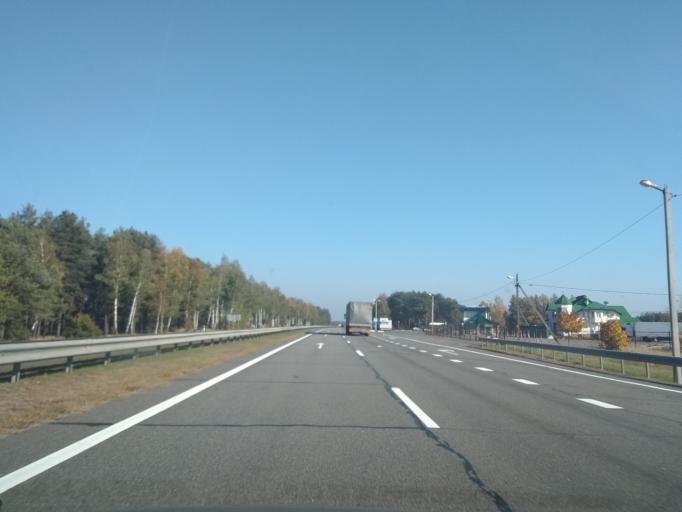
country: BY
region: Brest
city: Ivatsevichy
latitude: 52.7087
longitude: 25.3840
